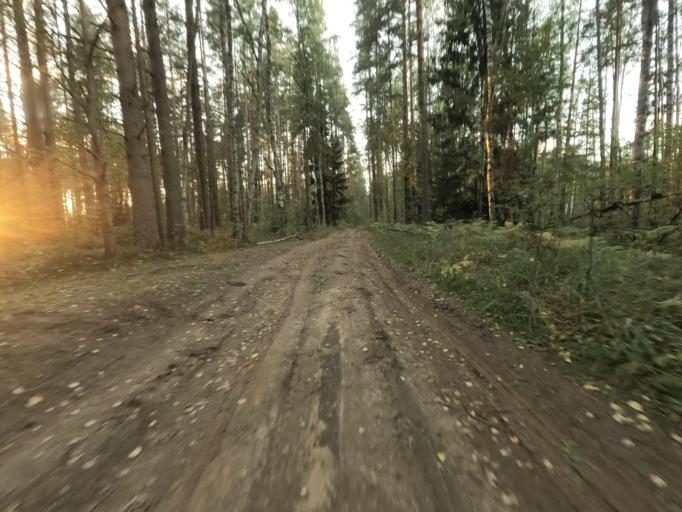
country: RU
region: Leningrad
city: Otradnoye
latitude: 59.8379
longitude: 30.8054
